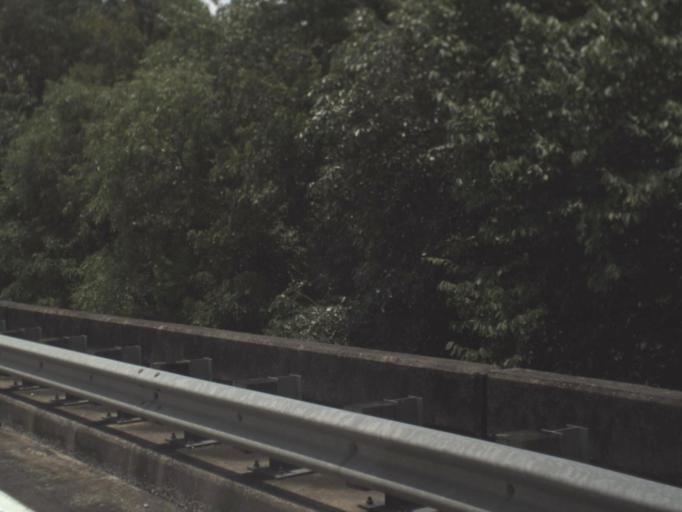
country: US
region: Florida
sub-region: Putnam County
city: Palatka
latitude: 29.4779
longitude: -81.7401
